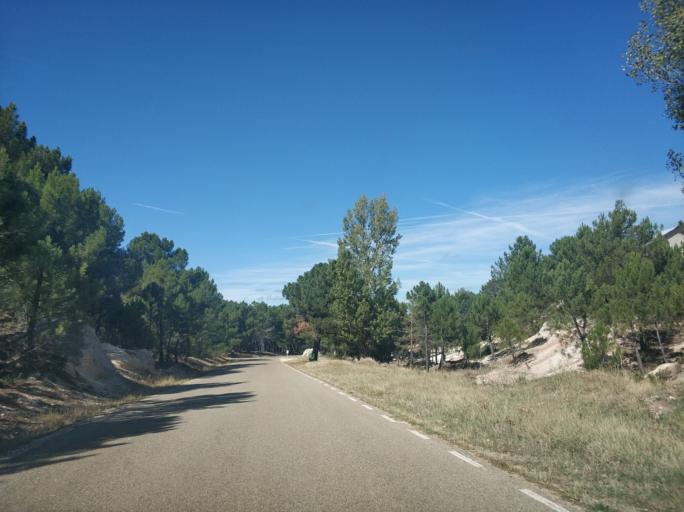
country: ES
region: Castille and Leon
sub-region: Provincia de Soria
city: Espeja de San Marcelino
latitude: 41.7942
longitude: -3.2133
